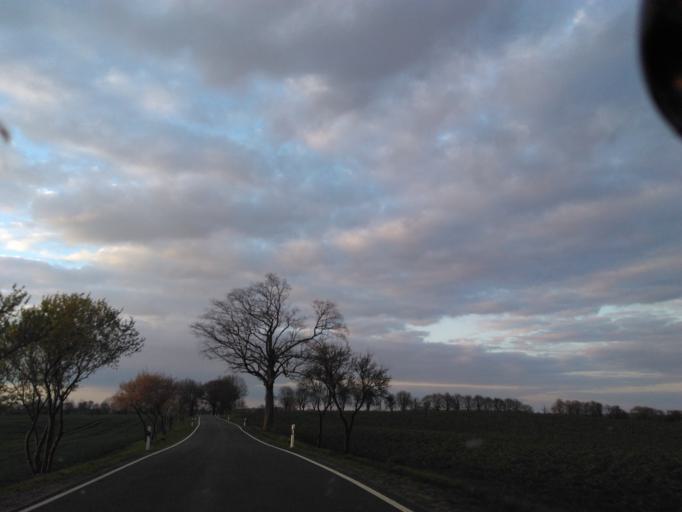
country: DE
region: Brandenburg
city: Buckow
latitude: 52.6258
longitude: 14.0692
